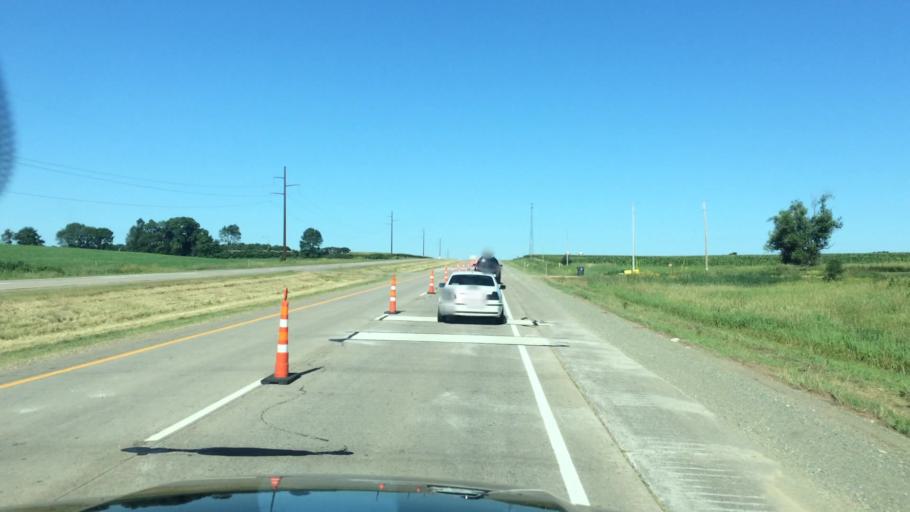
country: US
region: Wisconsin
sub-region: Marathon County
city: Marathon
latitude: 44.9446
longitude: -89.8905
